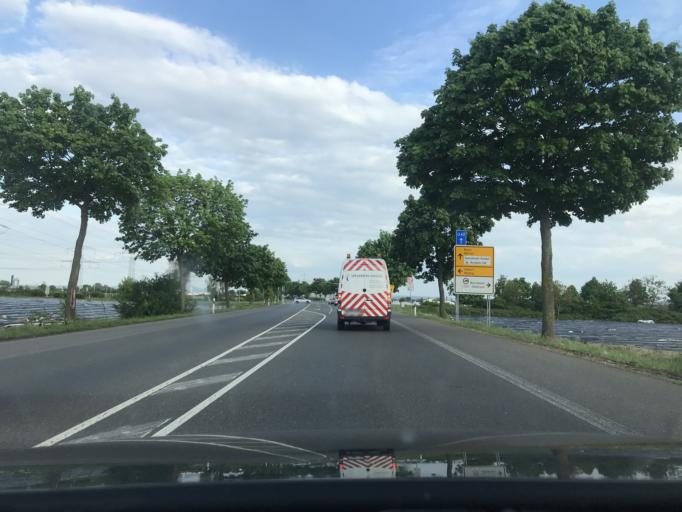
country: DE
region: North Rhine-Westphalia
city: Bornheim
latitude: 50.7695
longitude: 7.0034
